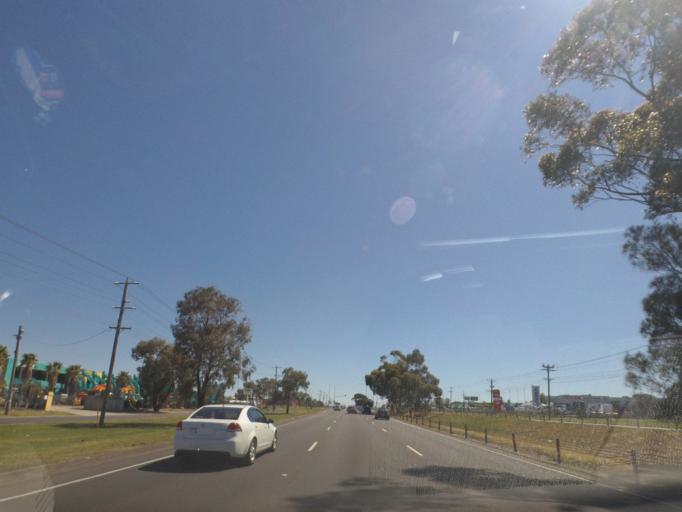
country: AU
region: Victoria
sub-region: Hume
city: Coolaroo
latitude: -37.6495
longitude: 144.9521
